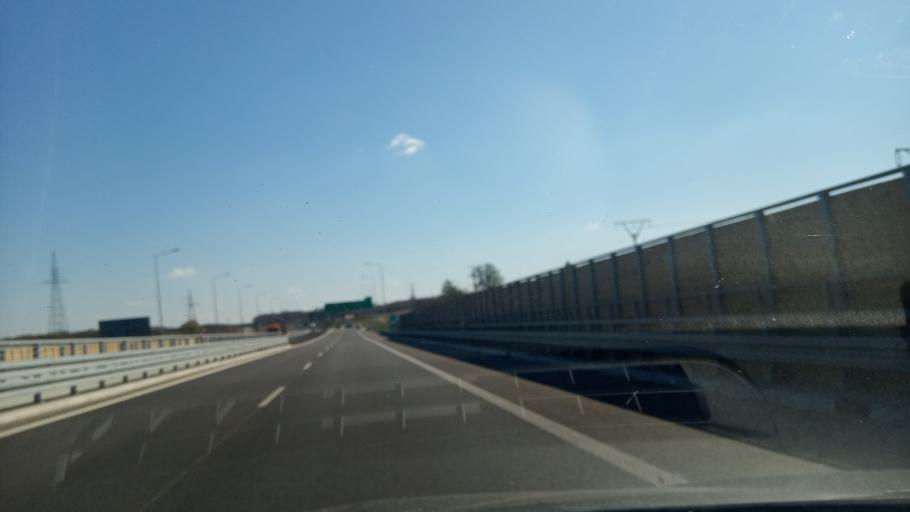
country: PL
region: West Pomeranian Voivodeship
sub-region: Powiat szczecinecki
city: Szczecinek
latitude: 53.6960
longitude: 16.7301
